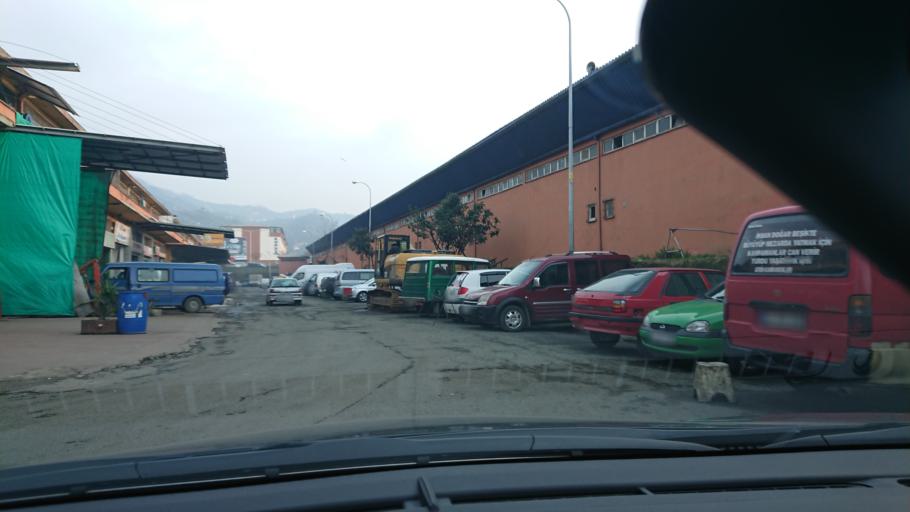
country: TR
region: Rize
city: Gundogdu
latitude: 41.0435
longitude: 40.5758
